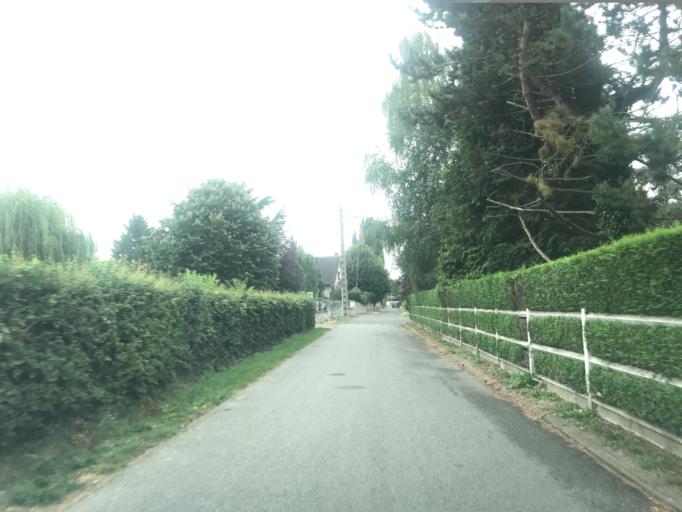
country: FR
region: Haute-Normandie
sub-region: Departement de l'Eure
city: Houlbec-Cocherel
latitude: 49.0734
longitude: 1.2878
